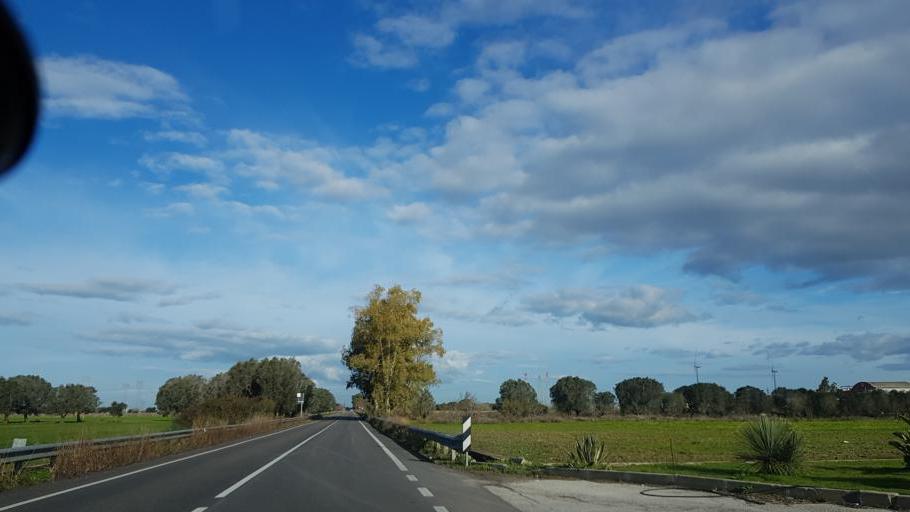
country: IT
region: Apulia
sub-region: Provincia di Brindisi
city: Tuturano
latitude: 40.5523
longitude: 17.9751
